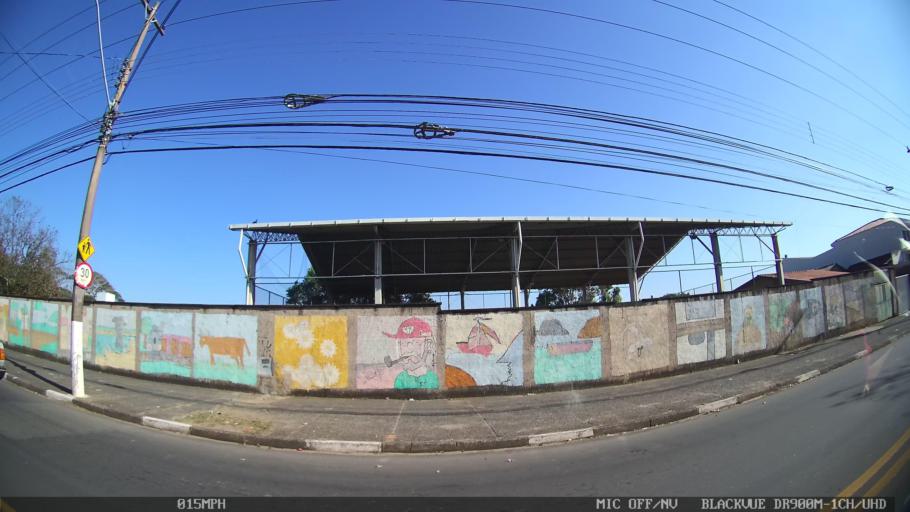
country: BR
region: Sao Paulo
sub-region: Campinas
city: Campinas
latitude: -22.9555
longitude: -47.1022
